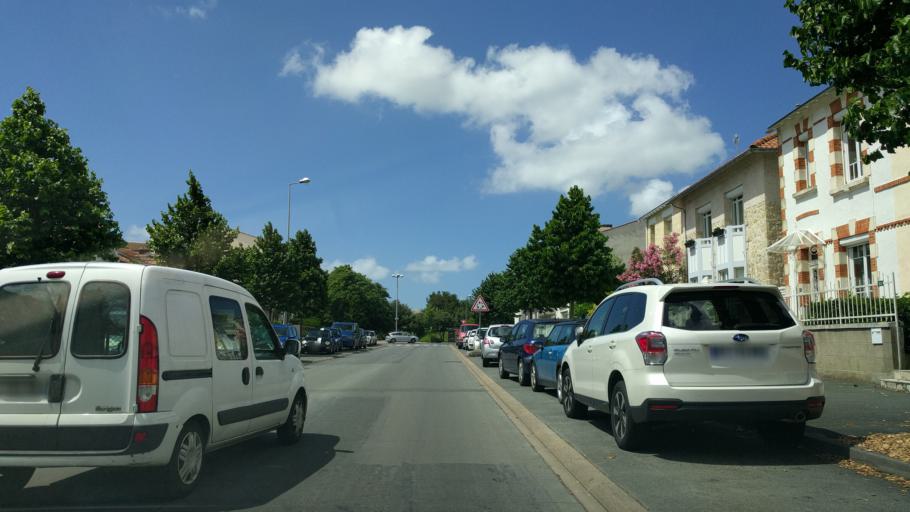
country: FR
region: Poitou-Charentes
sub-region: Departement de la Charente-Maritime
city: La Rochelle
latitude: 46.1628
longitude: -1.1402
